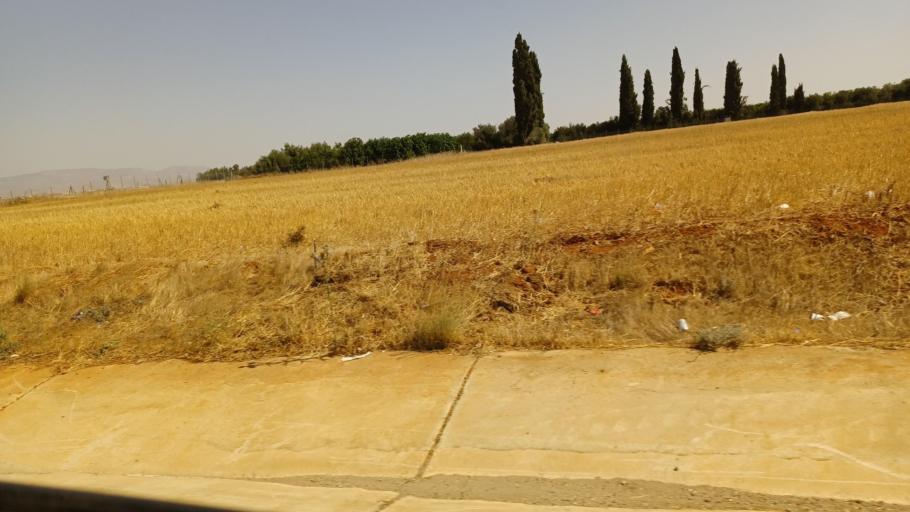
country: CY
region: Lefkosia
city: Akaki
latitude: 35.1413
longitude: 33.1565
